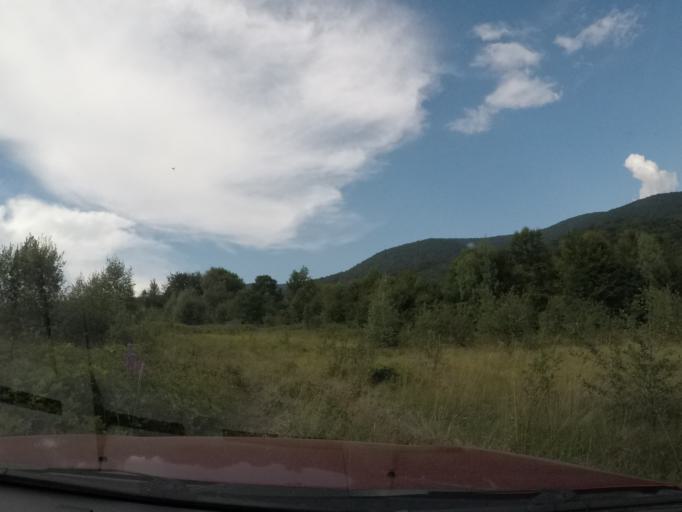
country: PL
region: Subcarpathian Voivodeship
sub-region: Powiat bieszczadzki
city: Lutowiska
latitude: 49.0348
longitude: 22.6391
